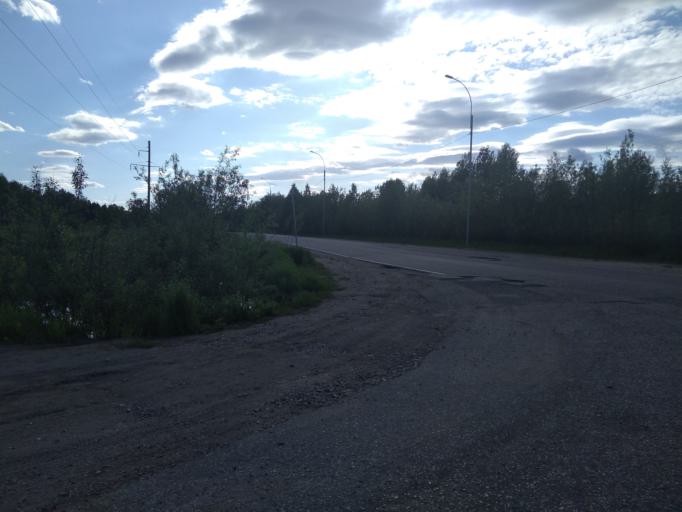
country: RU
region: Komi Republic
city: Pechora
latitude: 65.1371
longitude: 57.1540
